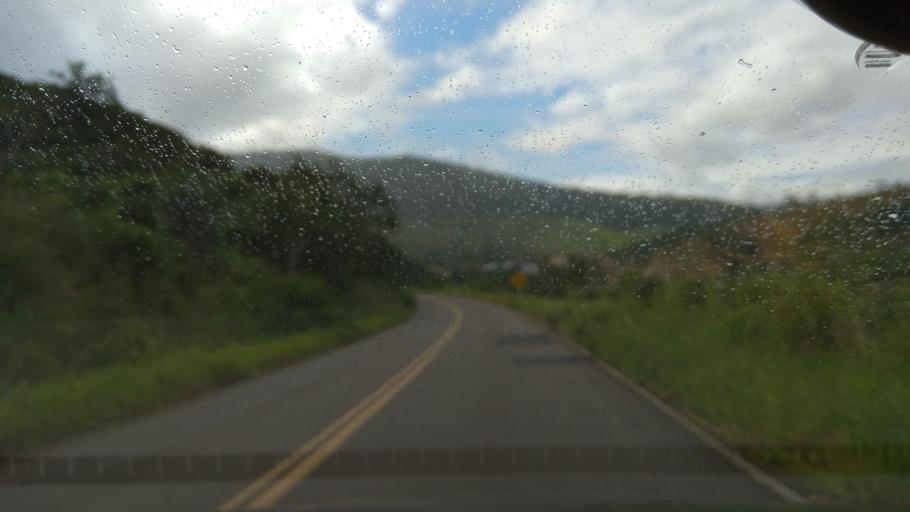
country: BR
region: Bahia
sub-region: Ubaira
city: Ubaira
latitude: -13.2510
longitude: -39.7225
